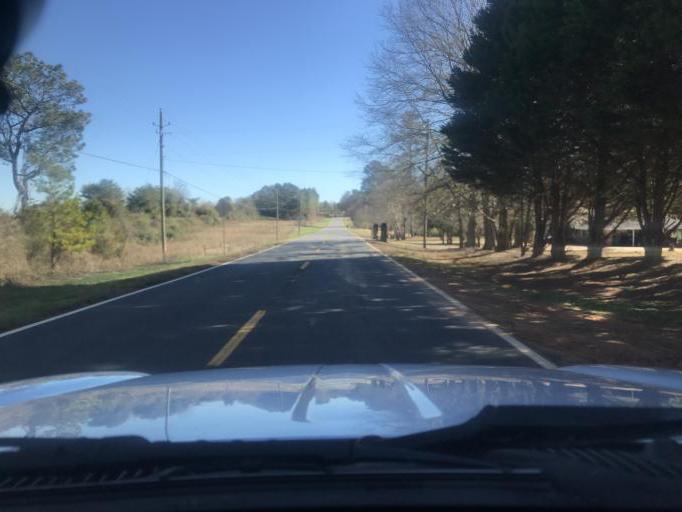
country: US
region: Georgia
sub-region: Barrow County
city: Russell
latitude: 33.9104
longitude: -83.7501
